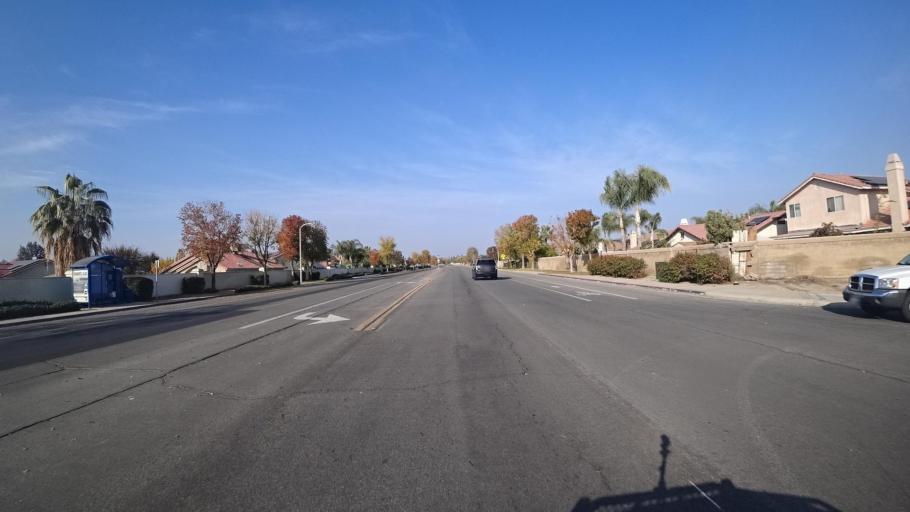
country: US
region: California
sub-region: Kern County
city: Delano
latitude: 35.7854
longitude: -119.2231
